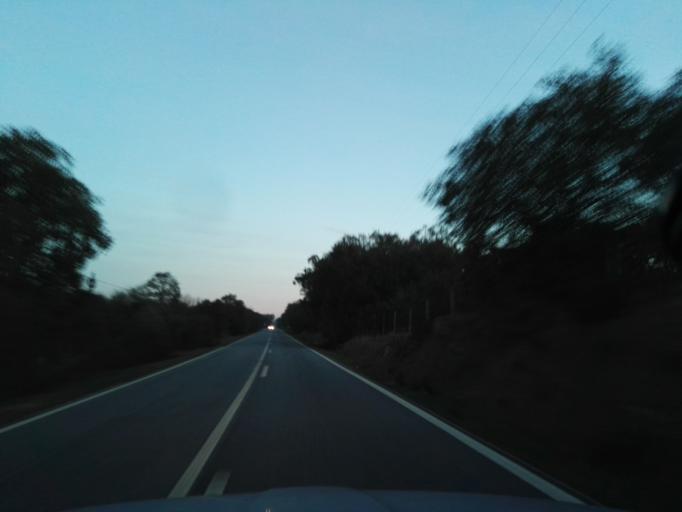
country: PT
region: Evora
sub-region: Arraiolos
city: Arraiolos
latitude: 38.7482
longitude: -8.0891
